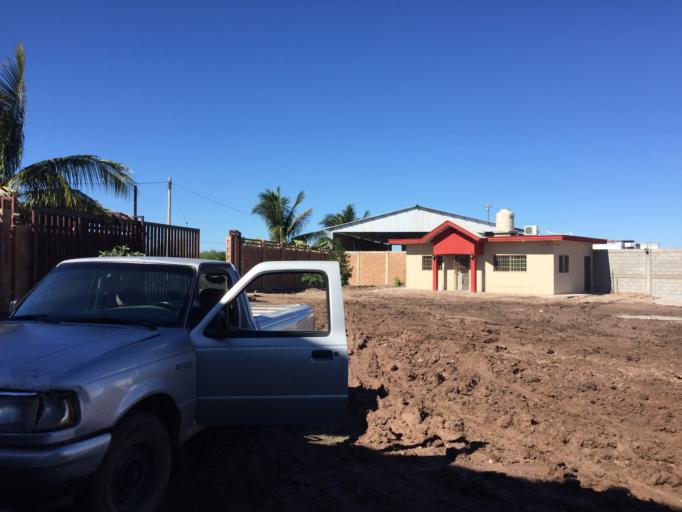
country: MX
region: Sinaloa
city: Villa de Costa Rica
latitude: 24.4991
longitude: -107.4320
